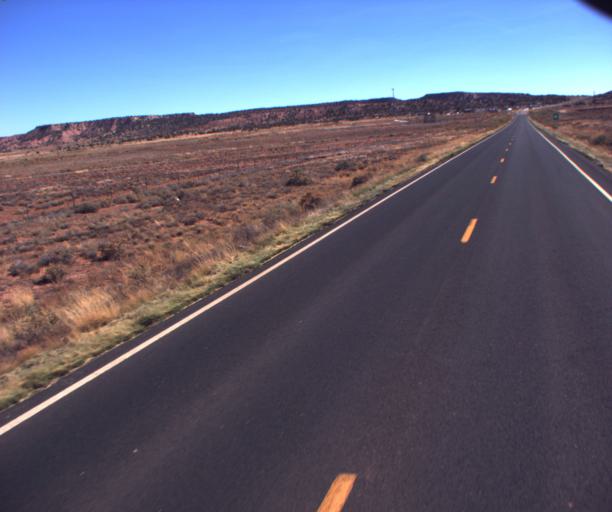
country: US
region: Arizona
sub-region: Apache County
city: Ganado
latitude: 35.7609
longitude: -109.6348
